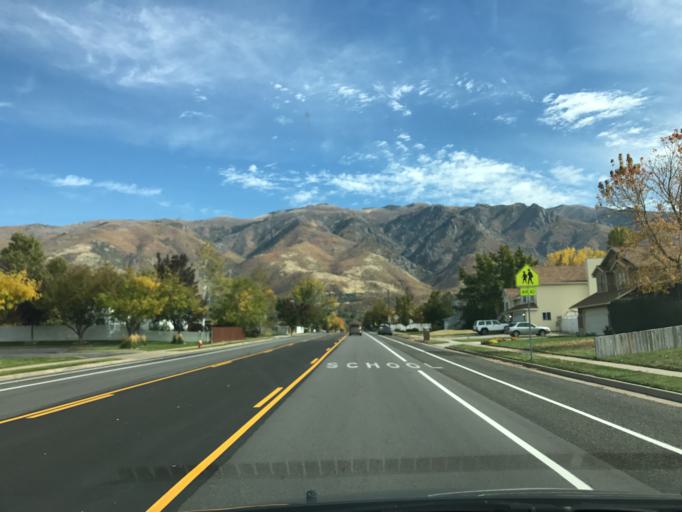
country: US
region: Utah
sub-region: Davis County
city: South Weber
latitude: 41.0891
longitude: -111.9281
